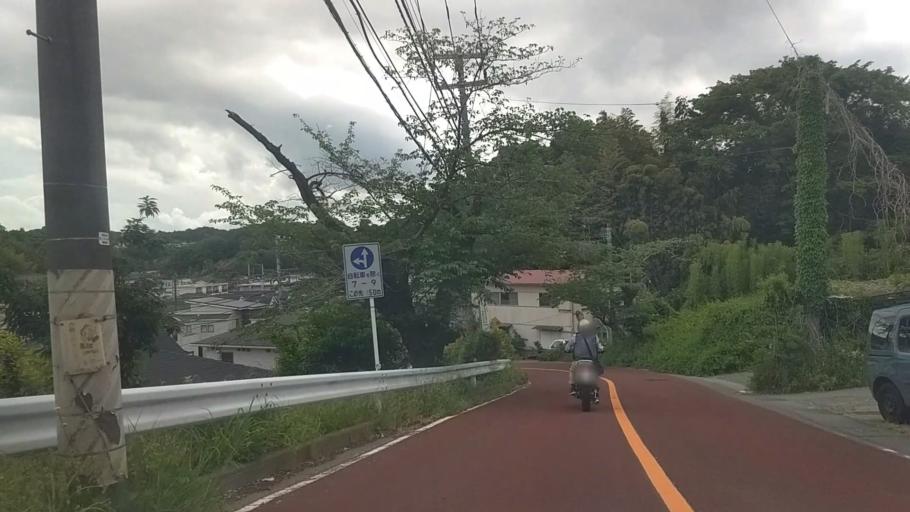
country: JP
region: Kanagawa
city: Kamakura
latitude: 35.3230
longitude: 139.5233
